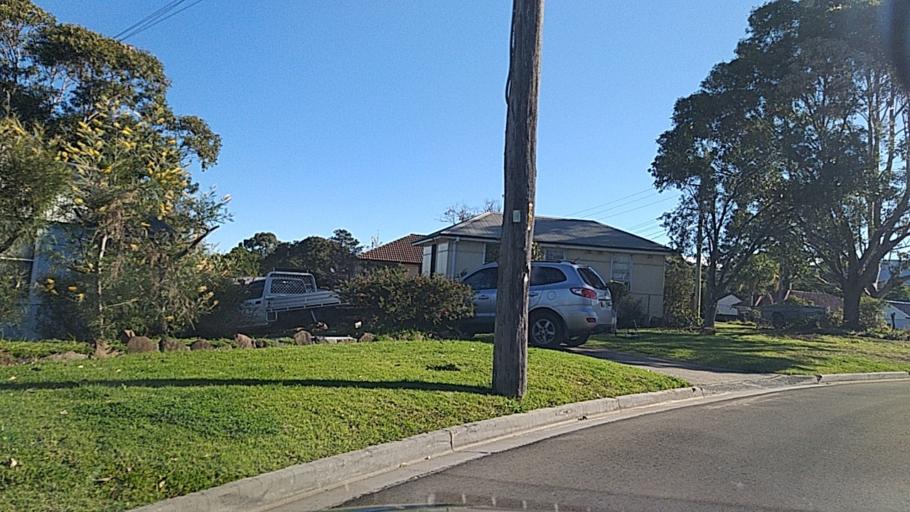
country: AU
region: New South Wales
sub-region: Wollongong
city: Cordeaux Heights
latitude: -34.4617
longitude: 150.8353
